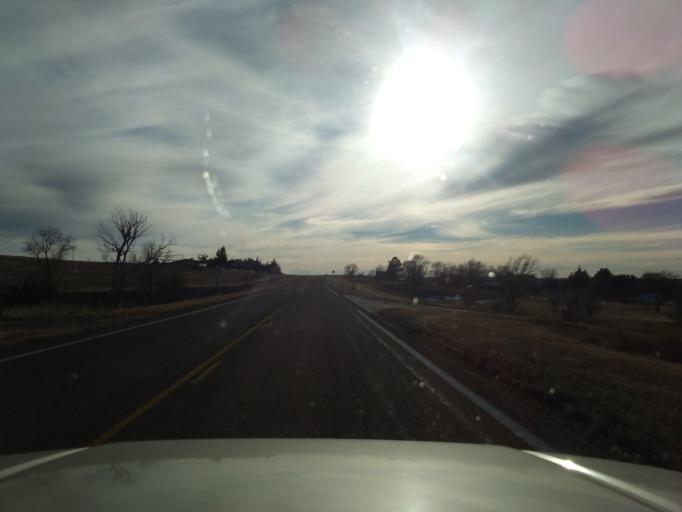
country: US
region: Kansas
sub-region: Norton County
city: Norton
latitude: 39.7375
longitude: -100.1737
